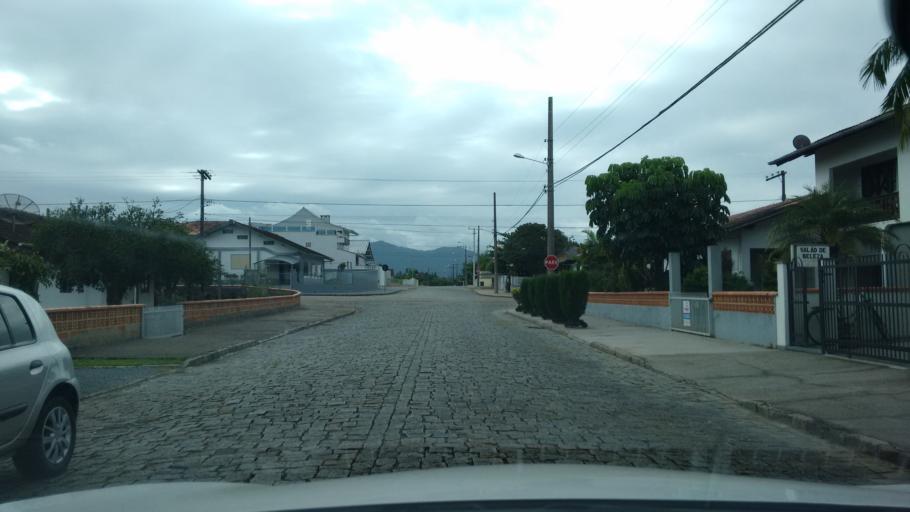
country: BR
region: Santa Catarina
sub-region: Timbo
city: Timbo
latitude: -26.8127
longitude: -49.2701
